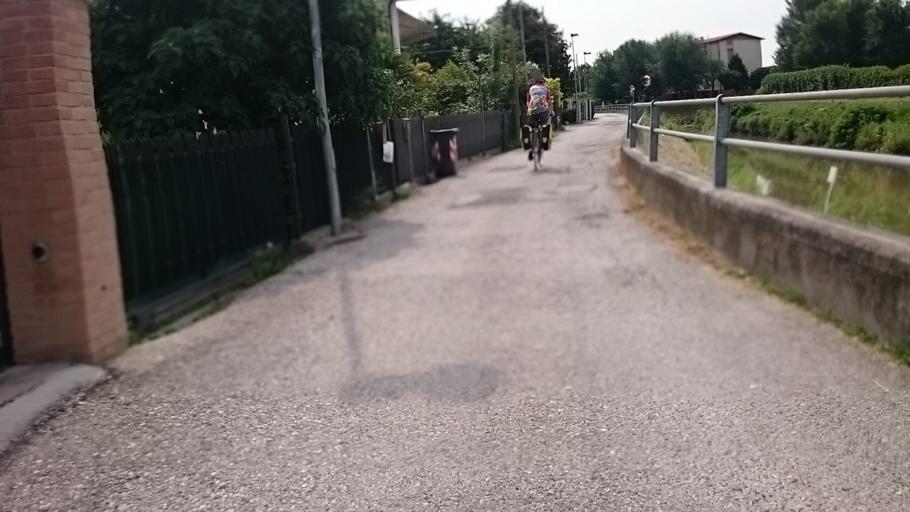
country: IT
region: Veneto
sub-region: Provincia di Venezia
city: Fornase
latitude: 45.4592
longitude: 12.1788
